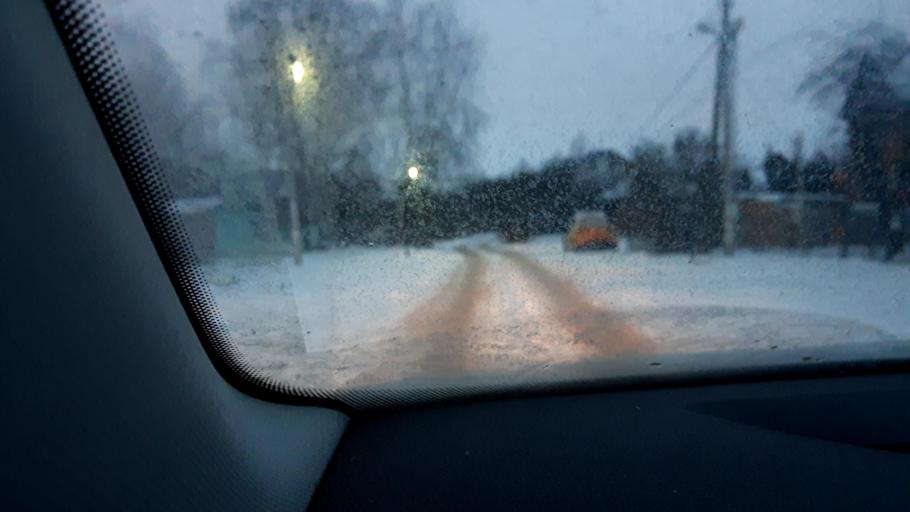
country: RU
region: Moskovskaya
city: Yam
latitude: 55.4828
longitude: 37.7170
